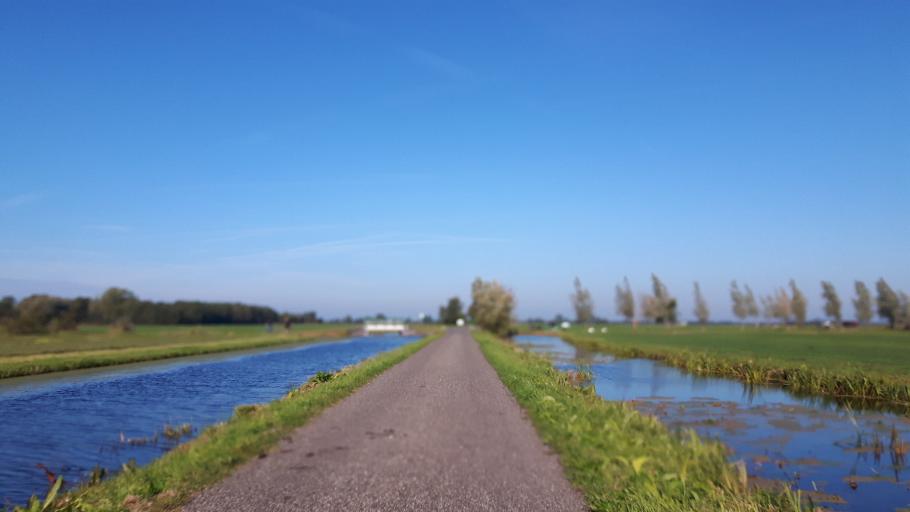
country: NL
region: South Holland
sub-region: Molenwaard
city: Liesveld
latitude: 51.9495
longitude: 4.8099
